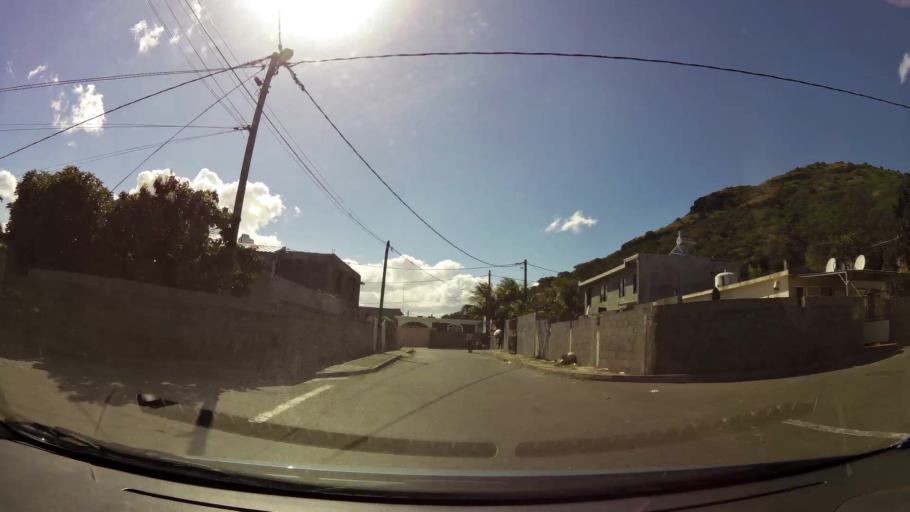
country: MU
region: Black River
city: Cascavelle
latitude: -20.2674
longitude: 57.4217
